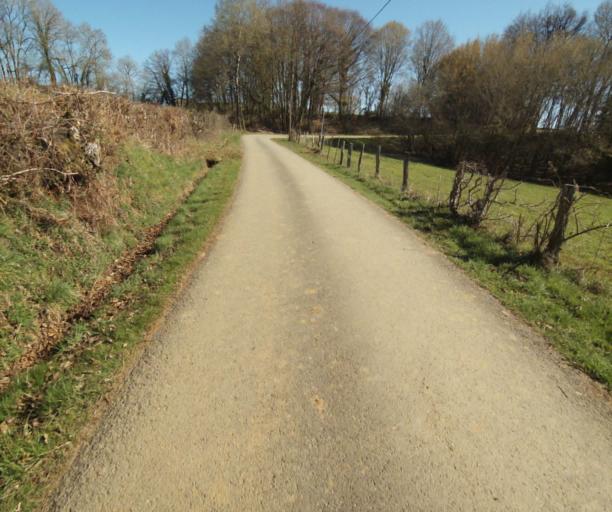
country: FR
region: Limousin
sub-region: Departement de la Correze
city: Chamboulive
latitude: 45.4171
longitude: 1.6715
